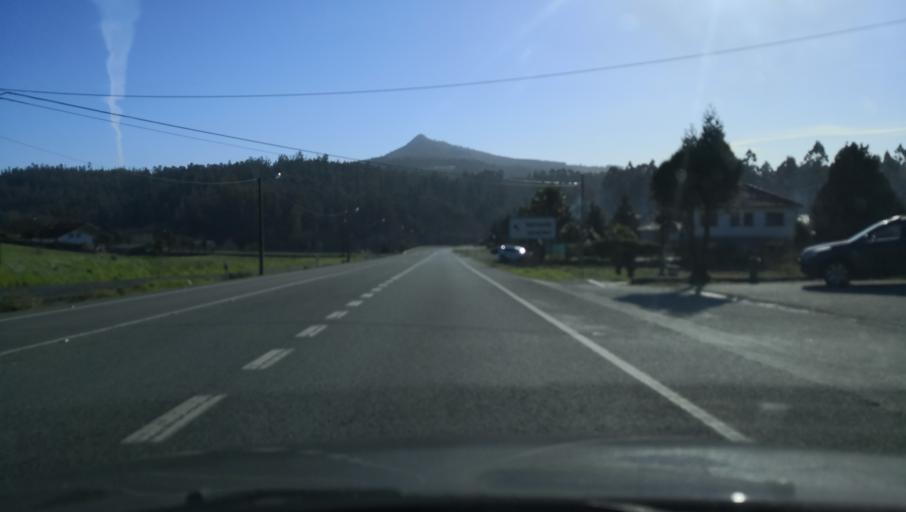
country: ES
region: Galicia
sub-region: Provincia da Coruna
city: Vedra
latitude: 42.8193
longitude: -8.4839
